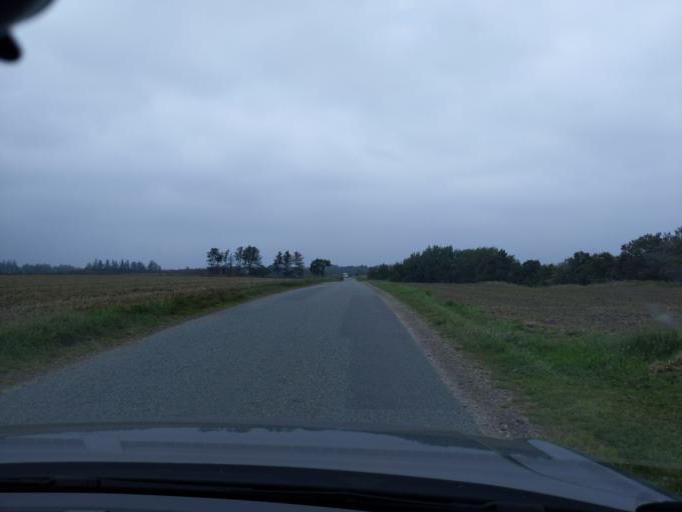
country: DK
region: Central Jutland
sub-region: Viborg Kommune
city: Stoholm
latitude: 56.4991
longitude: 9.2457
